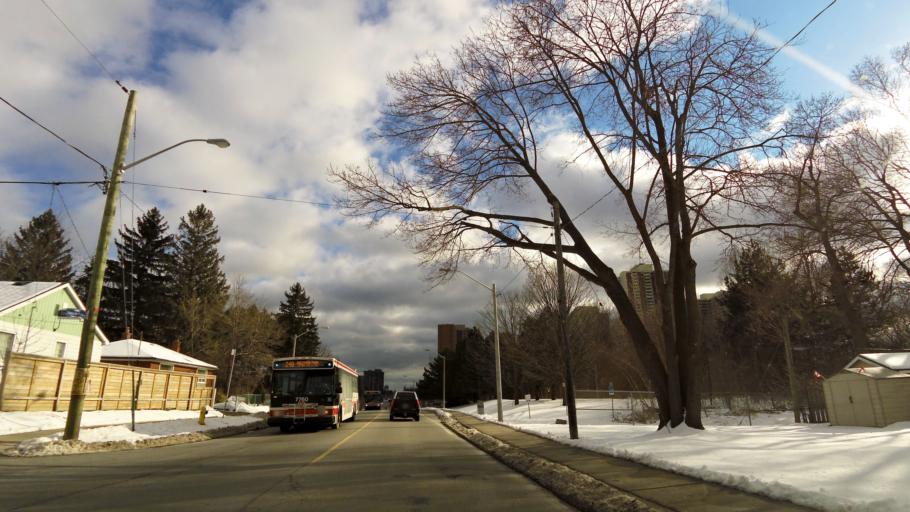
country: CA
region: Ontario
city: Scarborough
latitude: 43.7004
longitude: -79.2924
